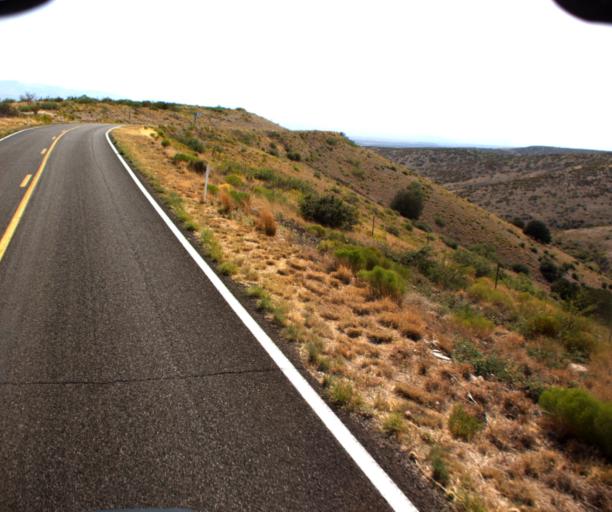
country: US
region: Arizona
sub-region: Greenlee County
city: Clifton
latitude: 33.0014
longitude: -109.1693
